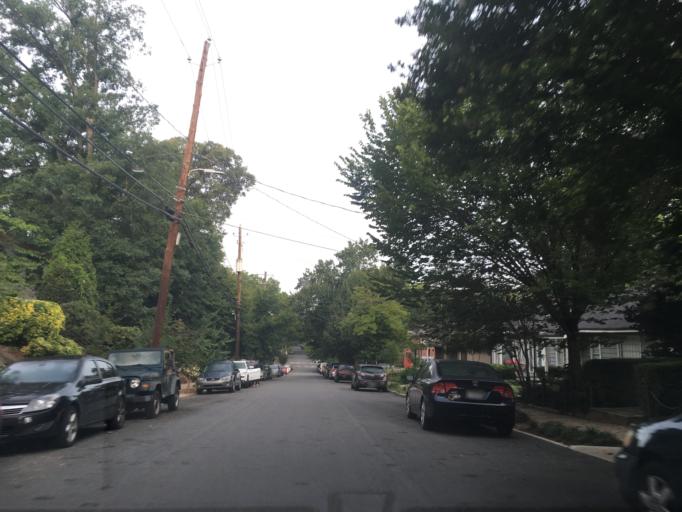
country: US
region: Georgia
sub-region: DeKalb County
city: Druid Hills
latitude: 33.7767
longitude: -84.3569
